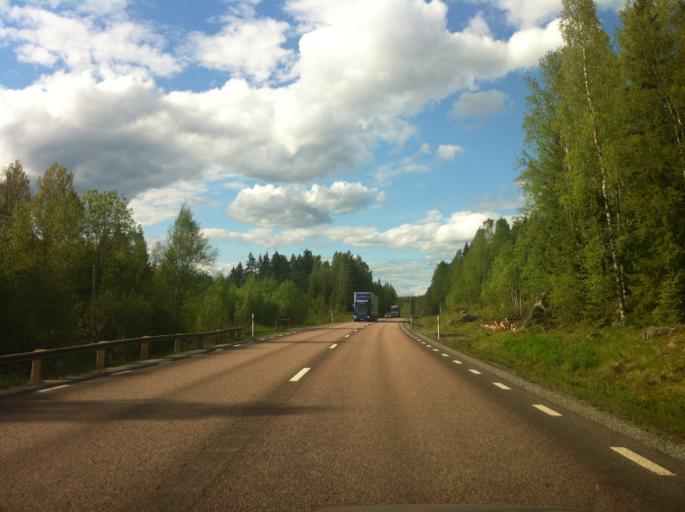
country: SE
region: Vaermland
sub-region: Filipstads Kommun
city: Filipstad
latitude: 59.6667
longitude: 14.2099
